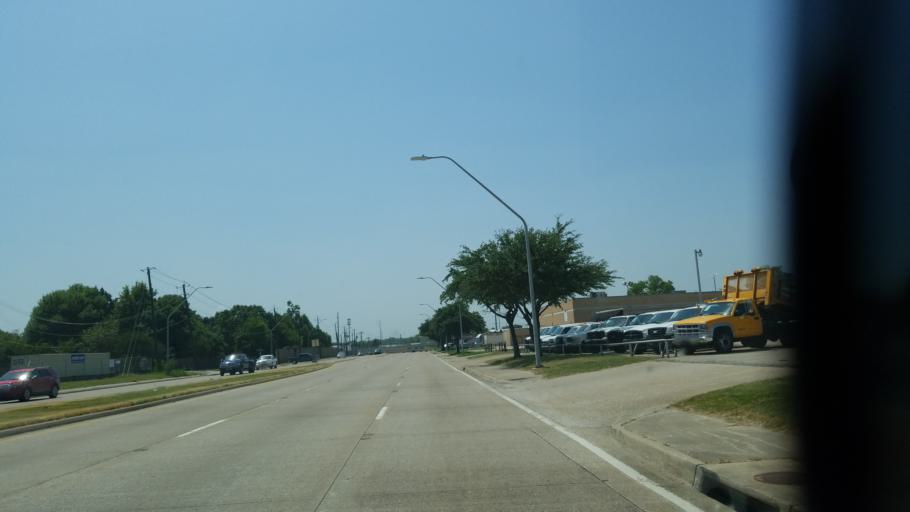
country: US
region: Texas
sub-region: Dallas County
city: Garland
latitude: 32.9201
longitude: -96.6280
